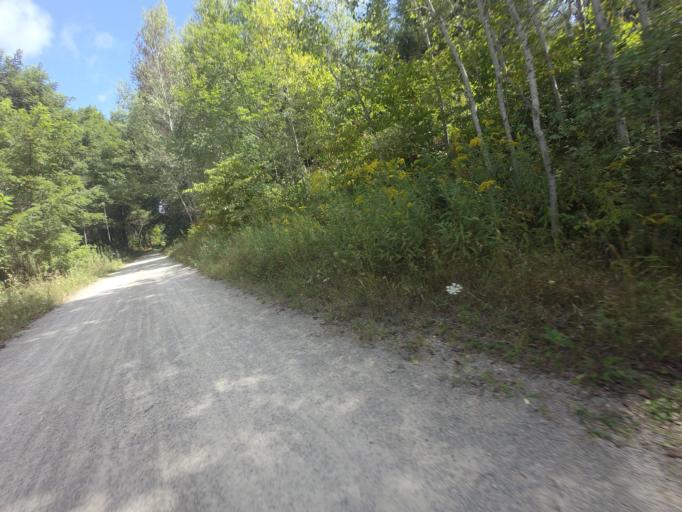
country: CA
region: Ontario
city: Uxbridge
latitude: 44.1277
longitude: -79.1046
